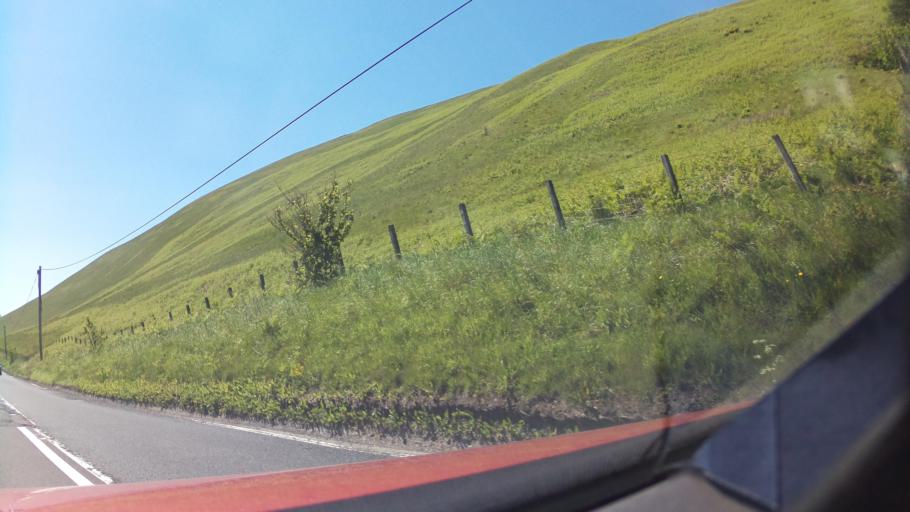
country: GB
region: Scotland
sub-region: Dumfries and Galloway
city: Langholm
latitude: 55.2402
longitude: -2.9721
